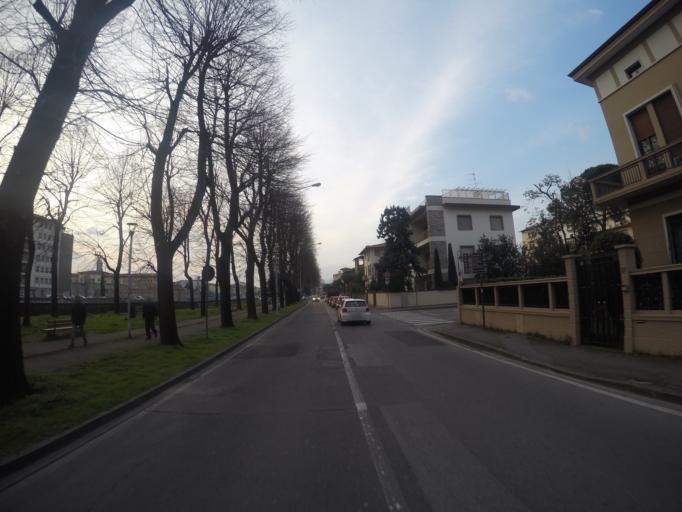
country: IT
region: Tuscany
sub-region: Provincia di Prato
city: Prato
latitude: 43.8789
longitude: 11.1063
